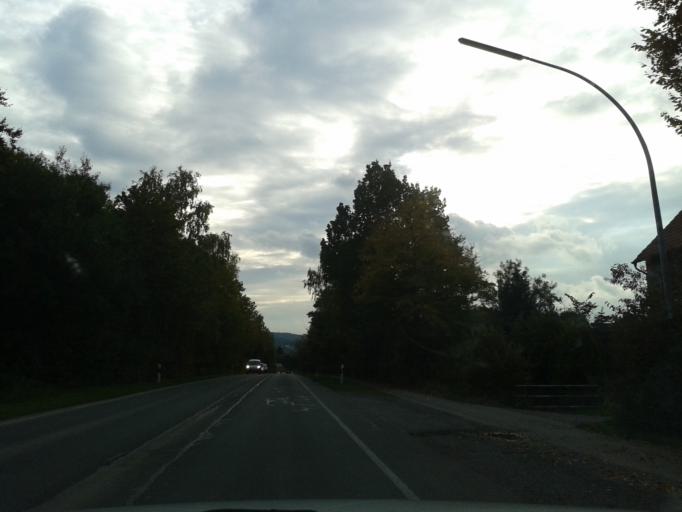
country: DE
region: North Rhine-Westphalia
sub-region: Regierungsbezirk Detmold
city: Horn-Bad Meinberg
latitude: 51.8870
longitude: 8.9648
